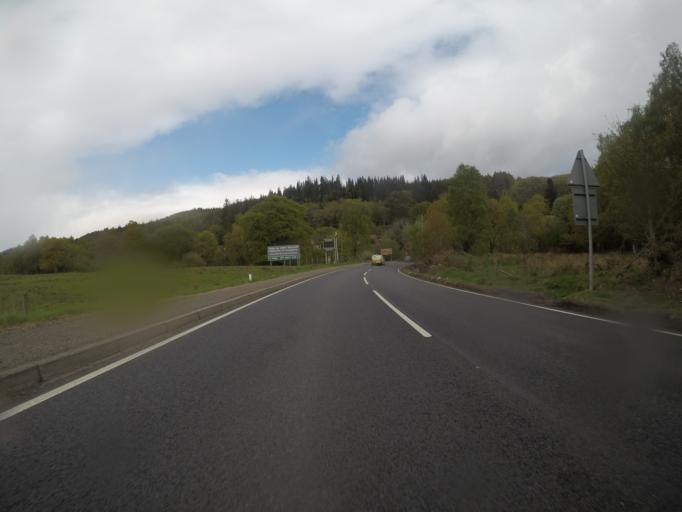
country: GB
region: Scotland
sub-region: Highland
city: Spean Bridge
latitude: 57.0681
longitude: -4.7926
